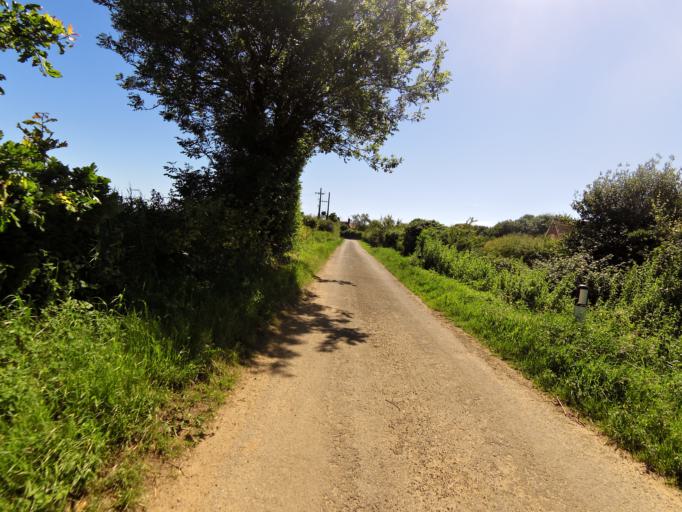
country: GB
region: England
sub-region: Suffolk
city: Felixstowe
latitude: 52.0094
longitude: 1.4220
